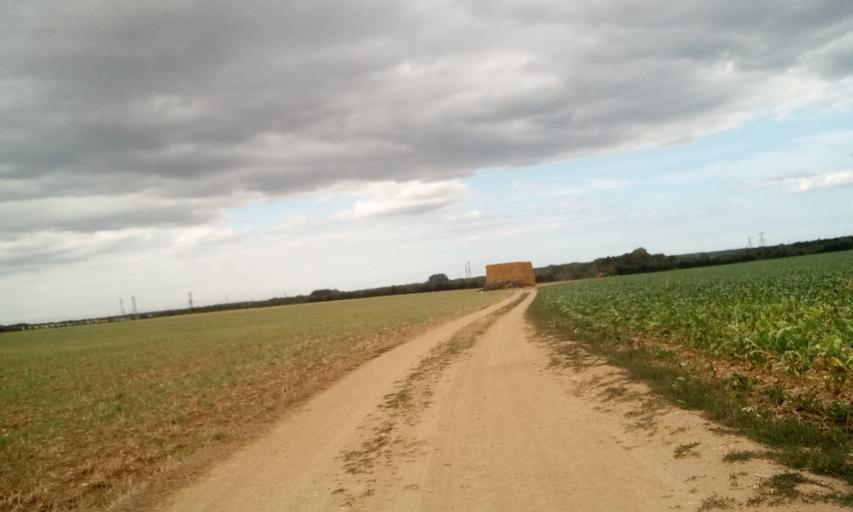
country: FR
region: Lower Normandy
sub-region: Departement du Calvados
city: Bellengreville
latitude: 49.1202
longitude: -0.2243
